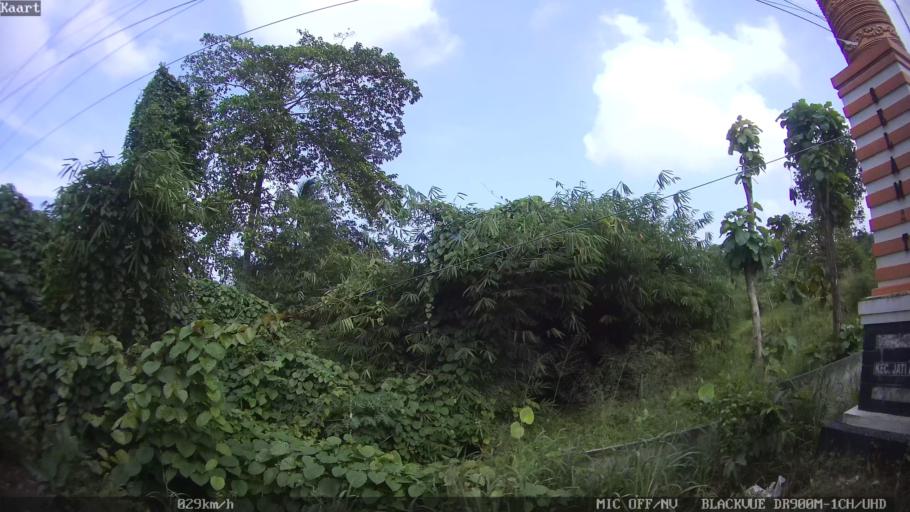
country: ID
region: Lampung
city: Kedaton
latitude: -5.3374
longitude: 105.2769
